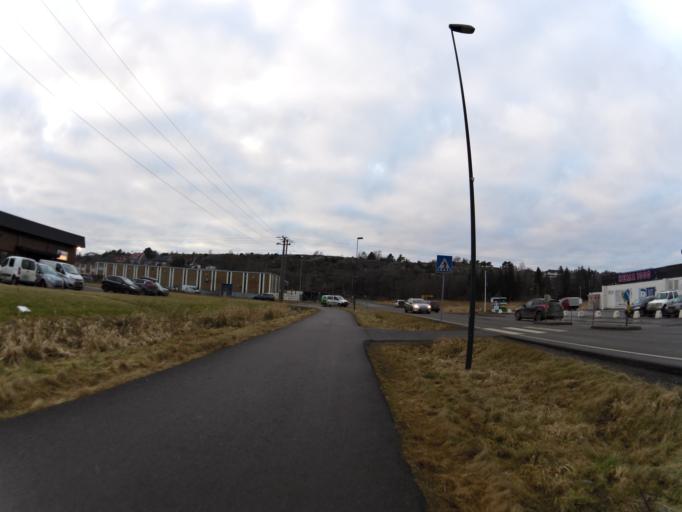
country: NO
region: Ostfold
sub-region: Fredrikstad
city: Fredrikstad
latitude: 59.2105
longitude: 10.8911
